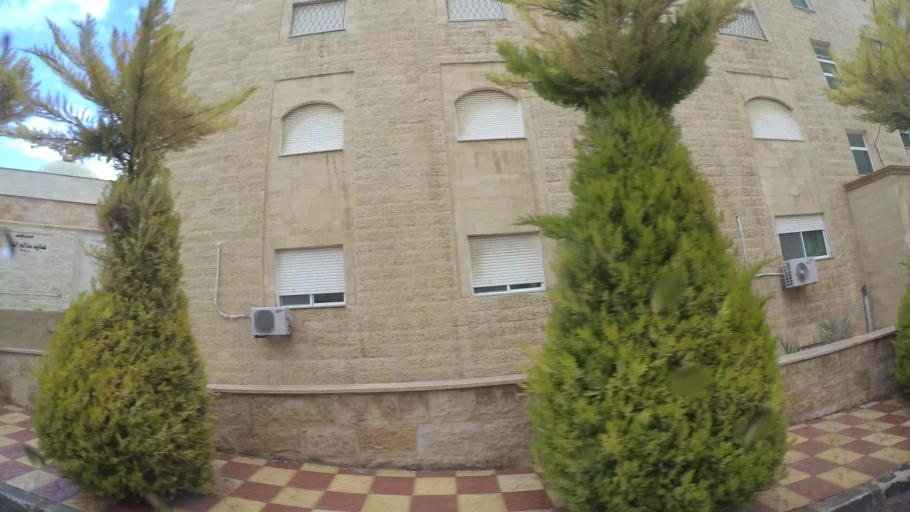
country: JO
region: Amman
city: Al Jubayhah
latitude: 32.0335
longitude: 35.8646
